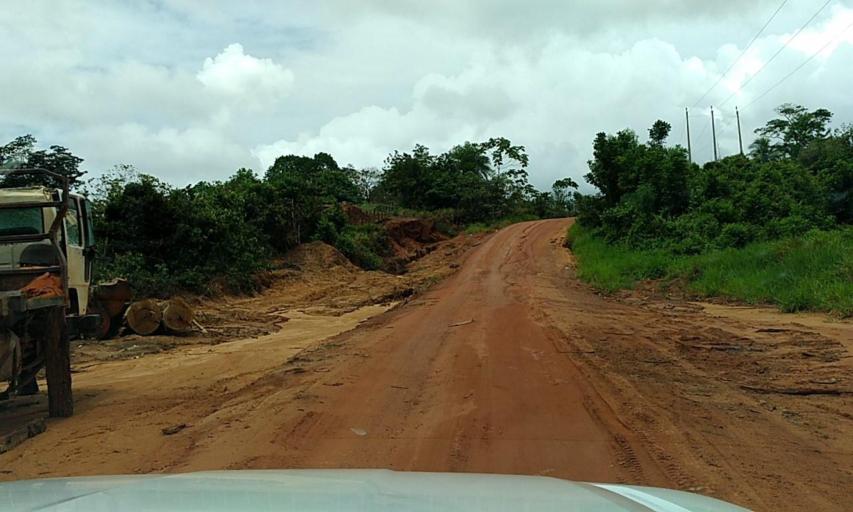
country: BR
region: Para
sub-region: Senador Jose Porfirio
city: Senador Jose Porfirio
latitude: -2.6155
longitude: -51.8712
